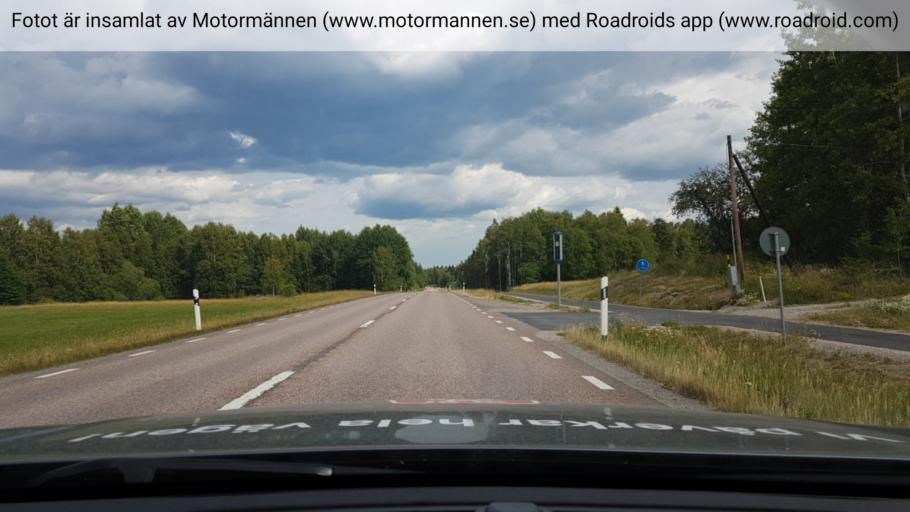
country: SE
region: Uppsala
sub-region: Heby Kommun
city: Morgongava
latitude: 59.9360
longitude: 16.9183
